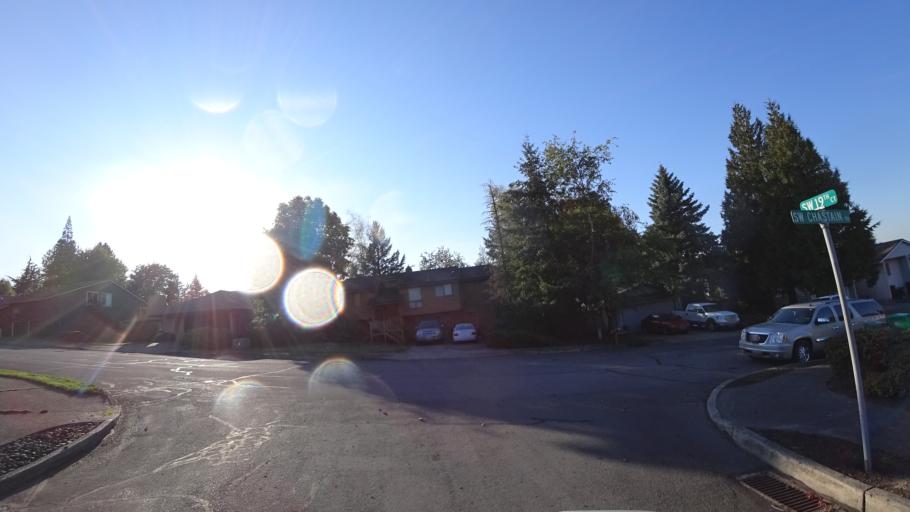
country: US
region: Oregon
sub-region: Multnomah County
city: Gresham
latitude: 45.4829
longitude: -122.4470
